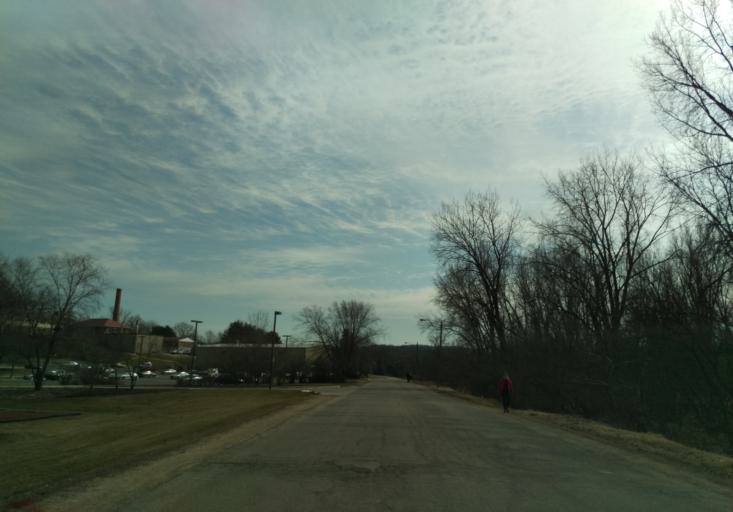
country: US
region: Iowa
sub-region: Winneshiek County
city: Decorah
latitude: 43.3116
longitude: -91.8091
